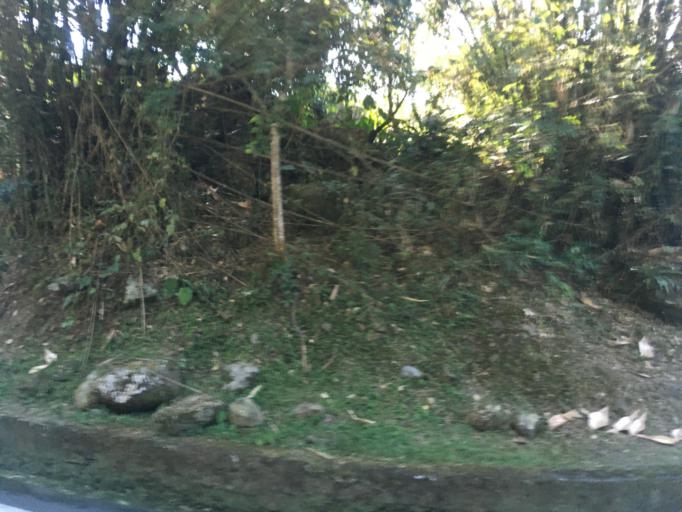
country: TW
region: Taiwan
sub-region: Chiayi
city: Jiayi Shi
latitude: 23.4206
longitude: 120.6440
